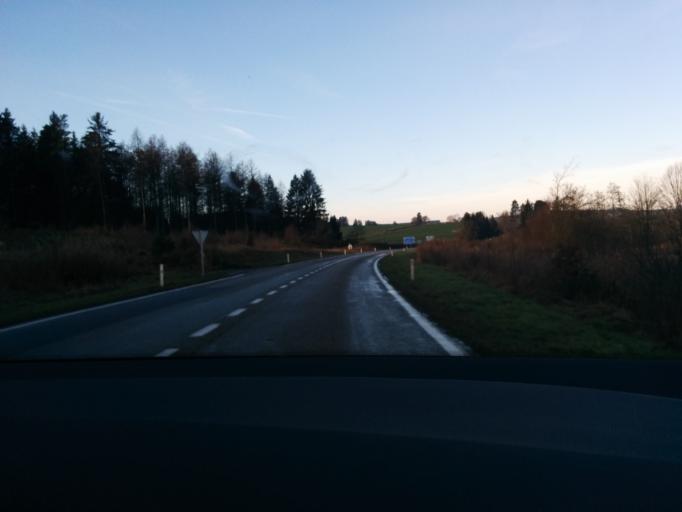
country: BE
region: Wallonia
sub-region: Province du Luxembourg
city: Gouvy
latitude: 50.2215
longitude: 5.9420
